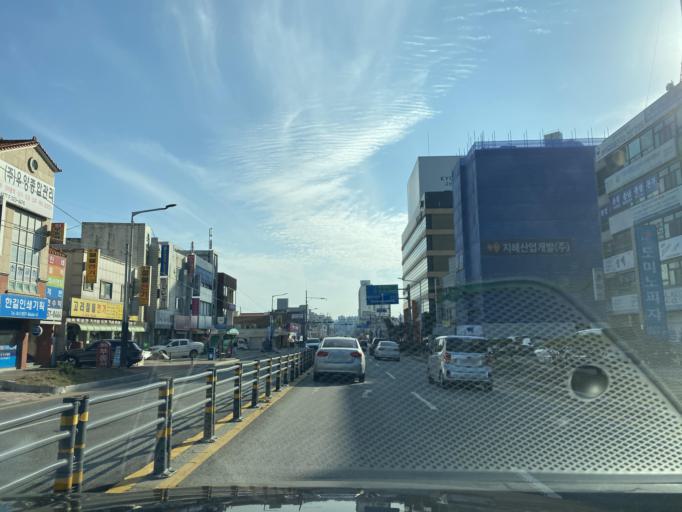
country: KR
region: Chungcheongnam-do
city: Cheonan
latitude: 36.8079
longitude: 127.1586
